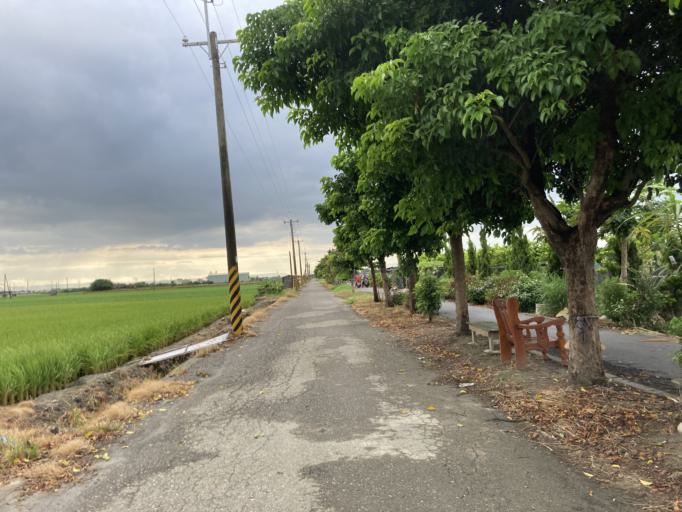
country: TW
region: Taiwan
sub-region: Yunlin
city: Douliu
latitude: 23.8788
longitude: 120.3637
